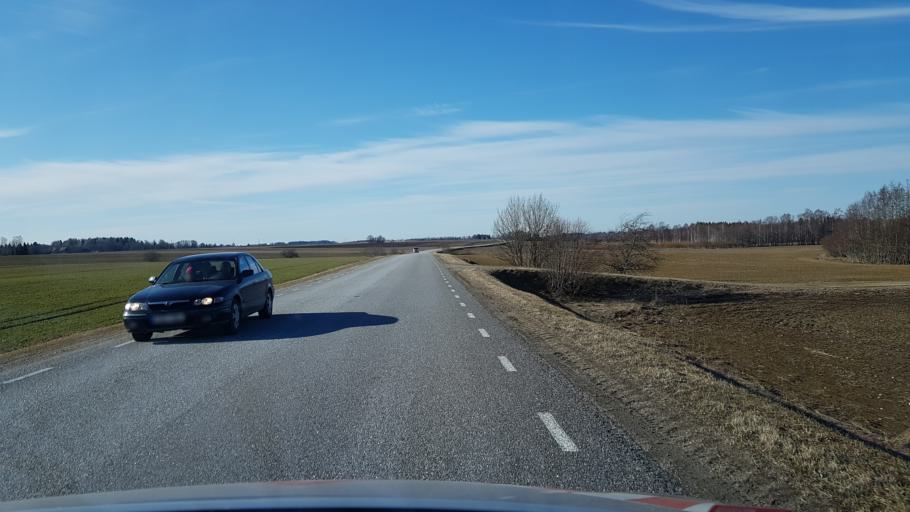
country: EE
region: Laeaene-Virumaa
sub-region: Kadrina vald
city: Kadrina
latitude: 59.3146
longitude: 26.1518
